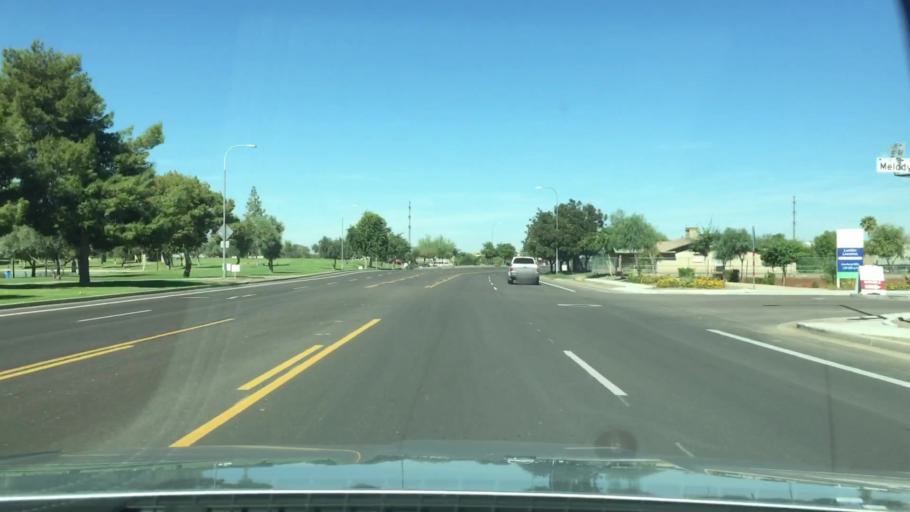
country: US
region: Arizona
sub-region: Maricopa County
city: Laveen
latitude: 33.3733
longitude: -112.1348
